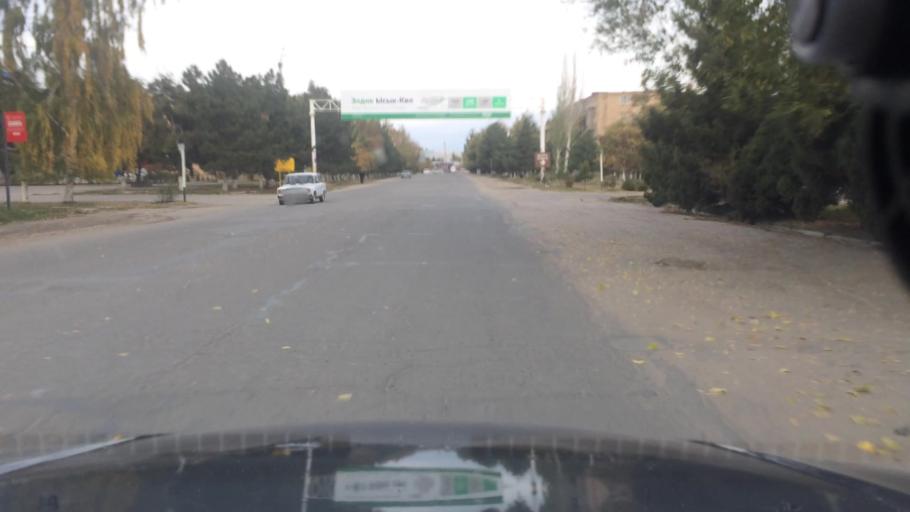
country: KG
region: Ysyk-Koel
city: Karakol
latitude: 42.4964
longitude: 78.3912
